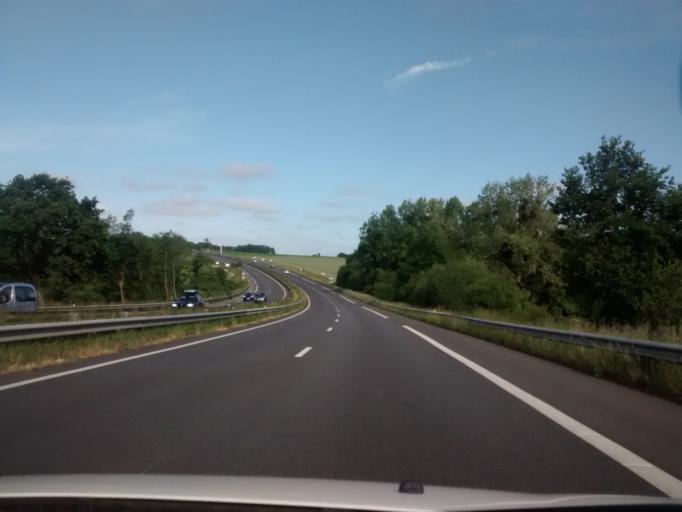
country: FR
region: Brittany
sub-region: Departement des Cotes-d'Armor
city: Lamballe
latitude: 48.4524
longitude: -2.4862
